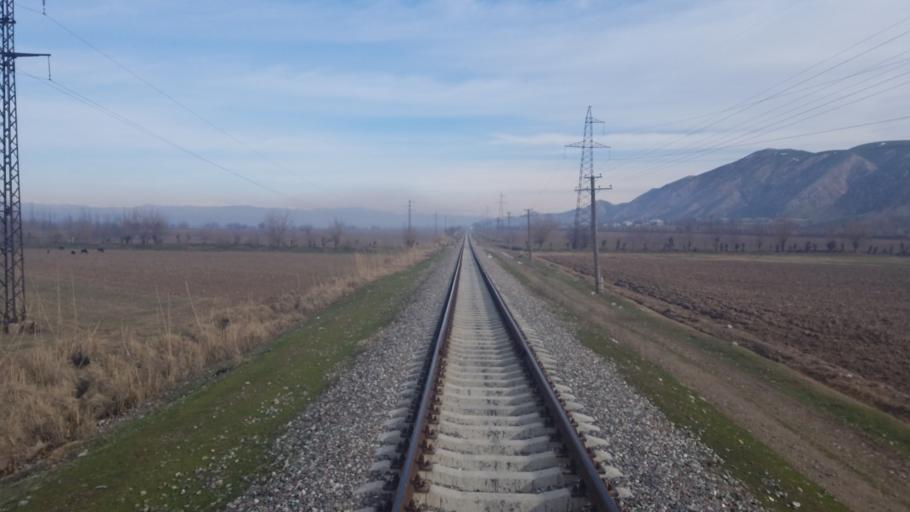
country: TJ
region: Khatlon
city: Sarband
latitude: 37.9176
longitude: 68.8804
